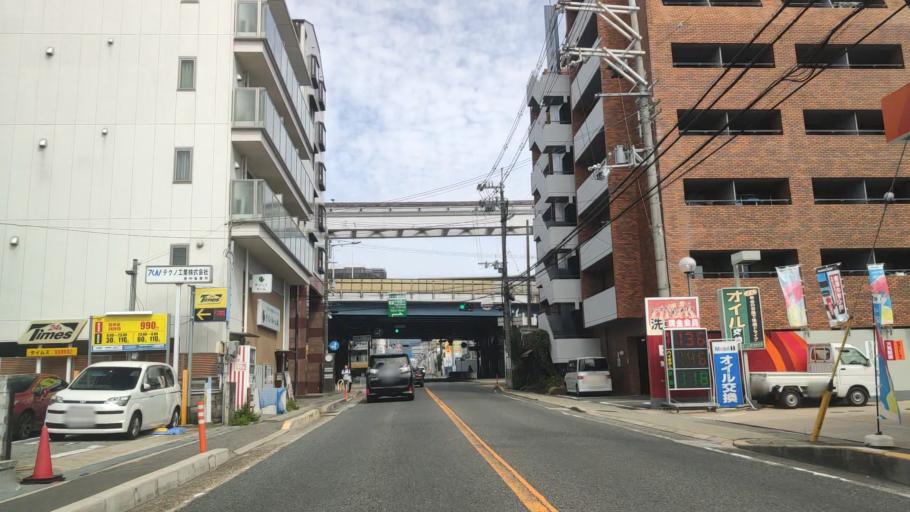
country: JP
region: Osaka
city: Toyonaka
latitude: 34.7995
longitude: 135.4485
